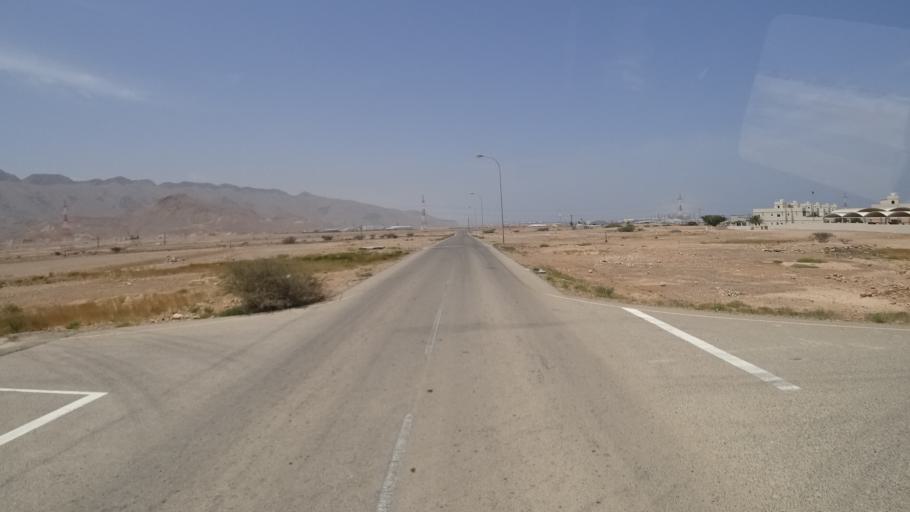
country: OM
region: Ash Sharqiyah
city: Sur
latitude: 22.6045
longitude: 59.4361
